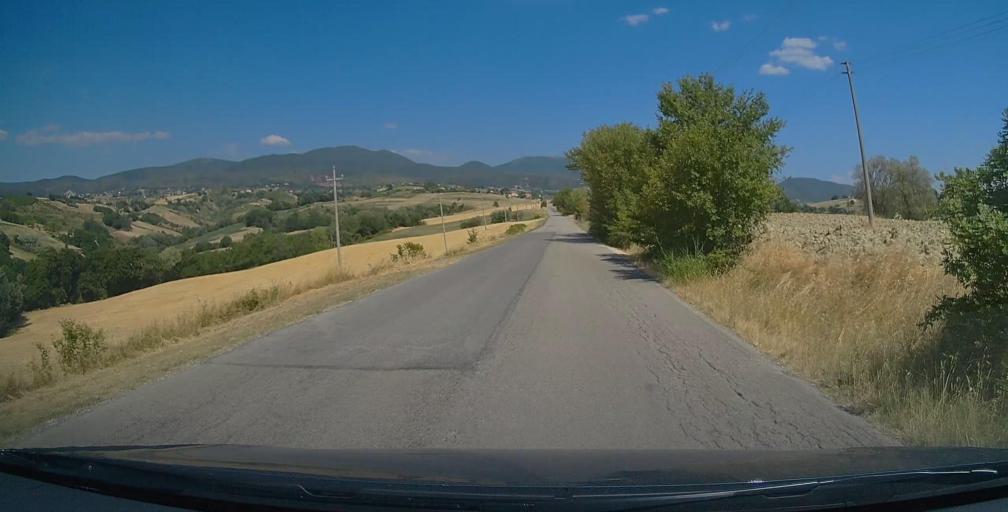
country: IT
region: Umbria
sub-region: Provincia di Terni
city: Otricoli
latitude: 42.4064
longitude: 12.5106
